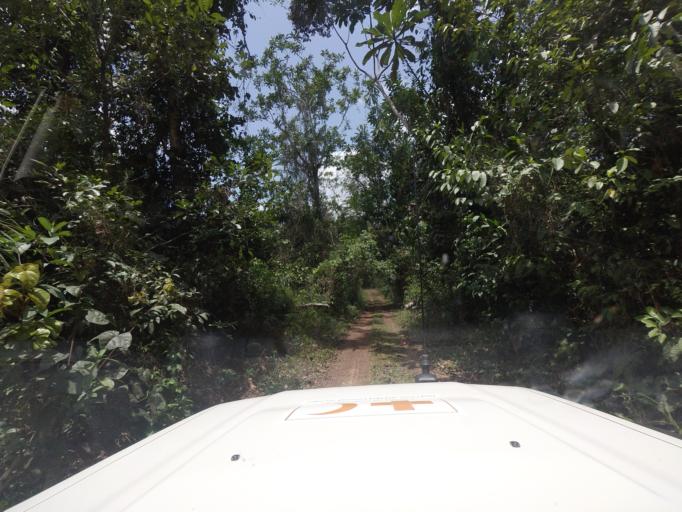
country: GN
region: Nzerekore
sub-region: Yomou
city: Yomou
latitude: 7.3744
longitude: -9.3143
